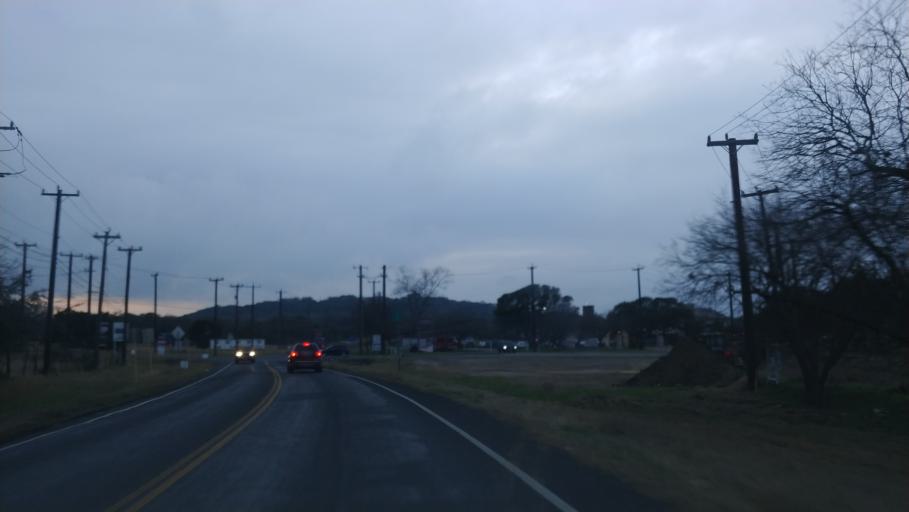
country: US
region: Texas
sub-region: Bexar County
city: Scenic Oaks
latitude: 29.6812
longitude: -98.6733
